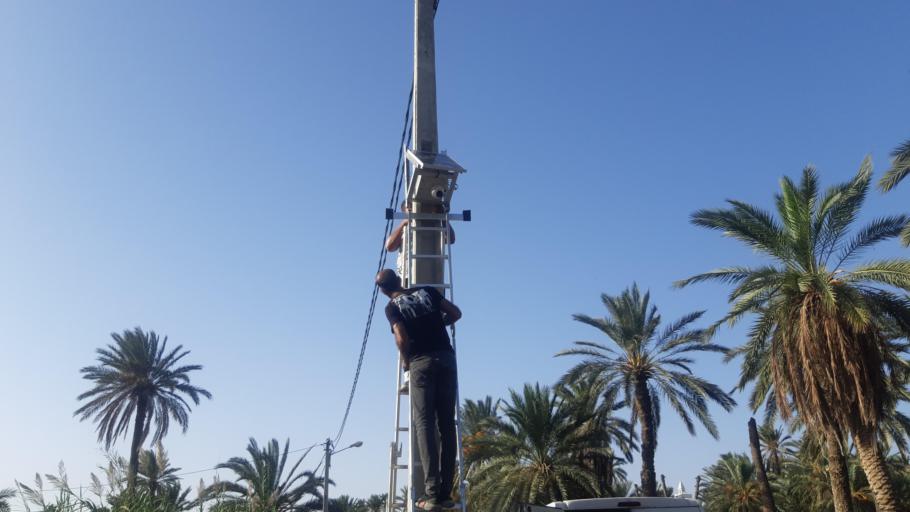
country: TN
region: Qabis
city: Gabes
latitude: 33.8632
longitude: 10.0614
